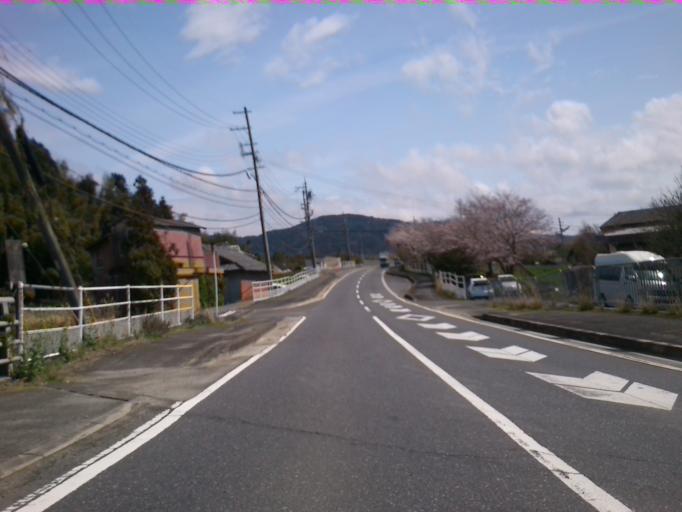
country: JP
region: Nara
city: Nara-shi
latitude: 34.7630
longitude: 135.8689
